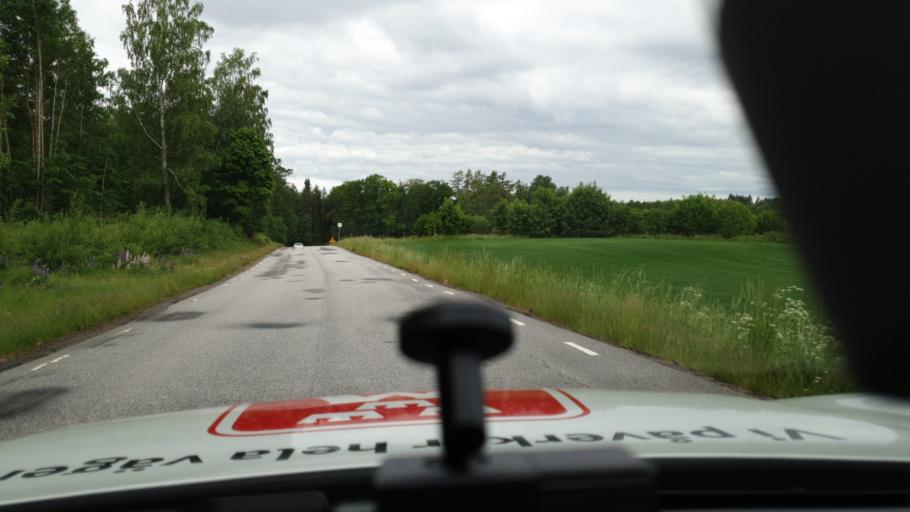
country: SE
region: Vaestra Goetaland
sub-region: Karlsborgs Kommun
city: Molltorp
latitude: 58.6814
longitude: 14.3505
